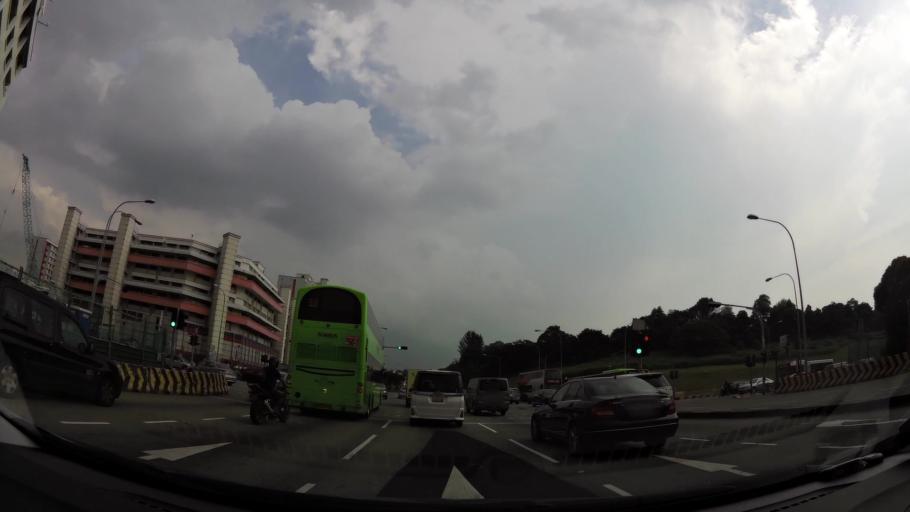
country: SG
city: Singapore
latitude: 1.3448
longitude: 103.9379
